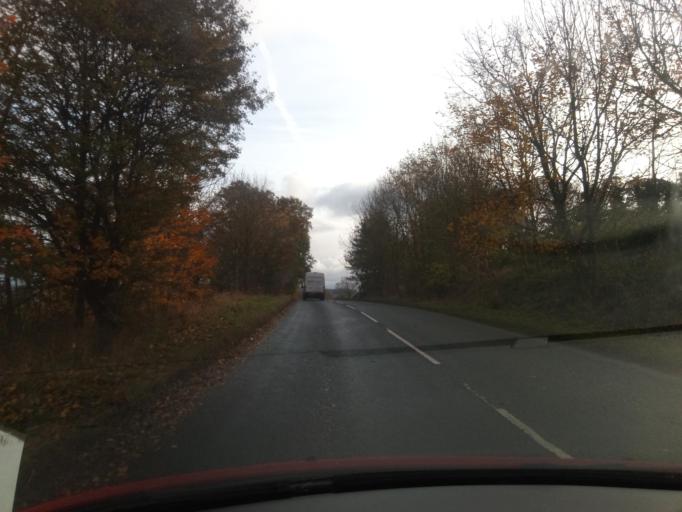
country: GB
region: England
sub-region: Northumberland
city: Birtley
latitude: 55.0458
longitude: -2.1533
